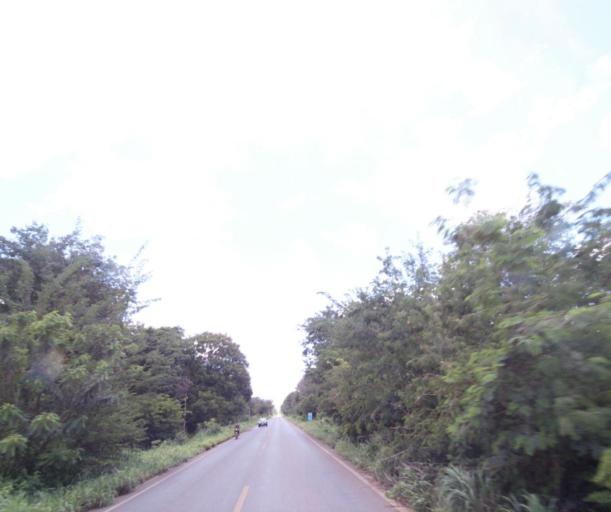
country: BR
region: Bahia
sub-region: Bom Jesus Da Lapa
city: Bom Jesus da Lapa
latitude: -13.2638
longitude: -43.5603
